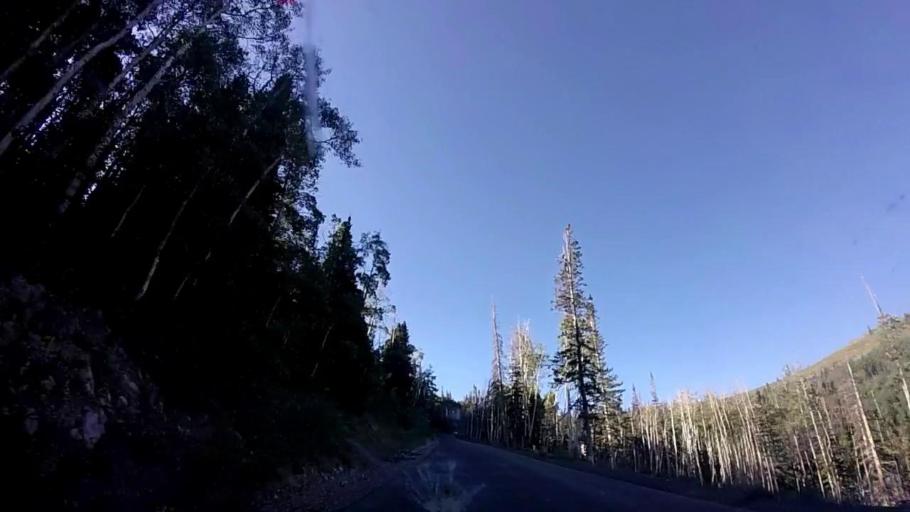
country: US
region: Utah
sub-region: Summit County
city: Park City
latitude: 40.6117
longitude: -111.5068
